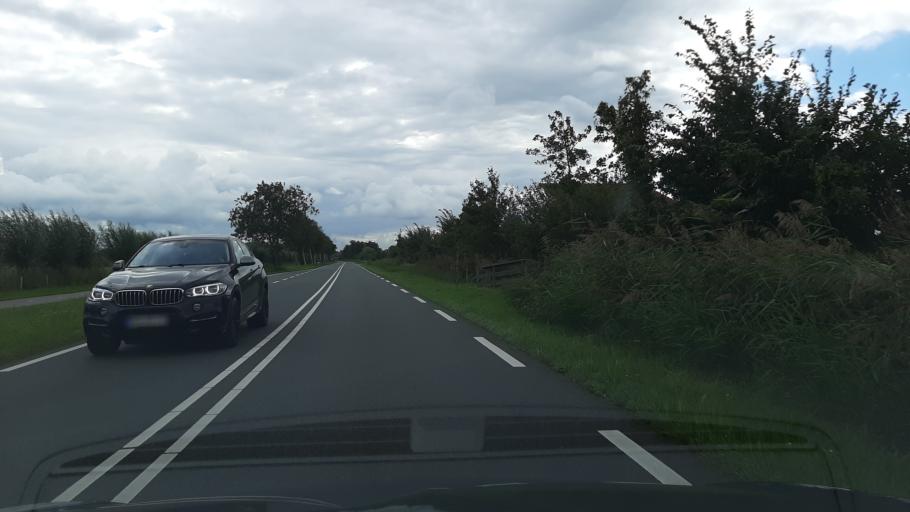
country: NL
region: Overijssel
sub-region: Gemeente Steenwijkerland
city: Giethoorn
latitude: 52.7019
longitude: 6.0719
